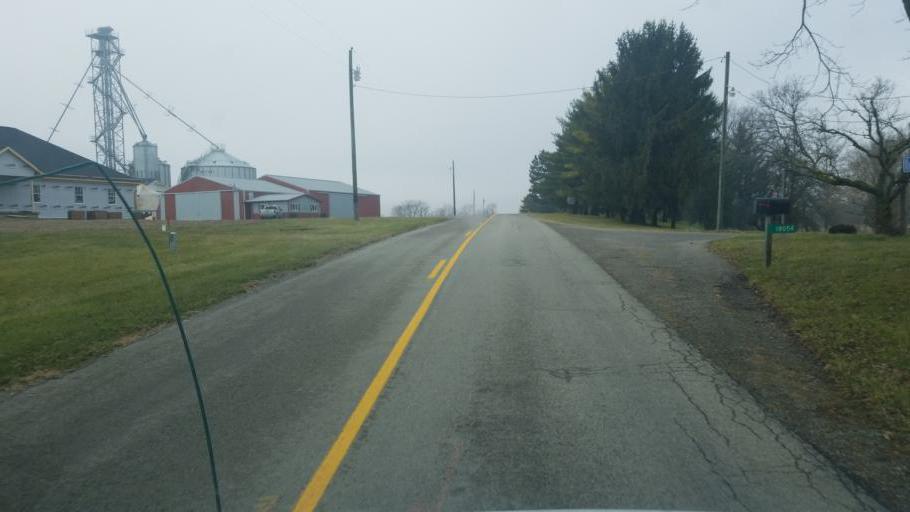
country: US
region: Ohio
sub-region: Champaign County
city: North Lewisburg
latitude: 40.2520
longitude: -83.5423
